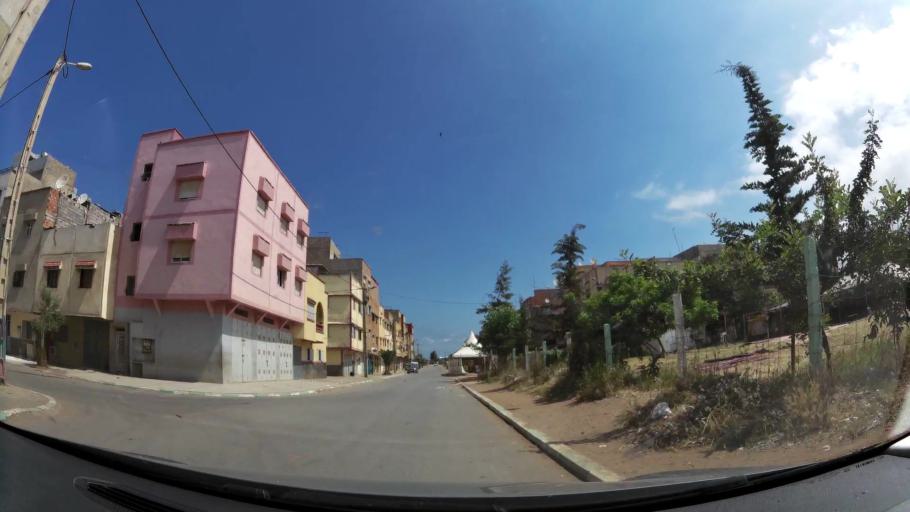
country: MA
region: Rabat-Sale-Zemmour-Zaer
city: Sale
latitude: 34.0669
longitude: -6.7812
